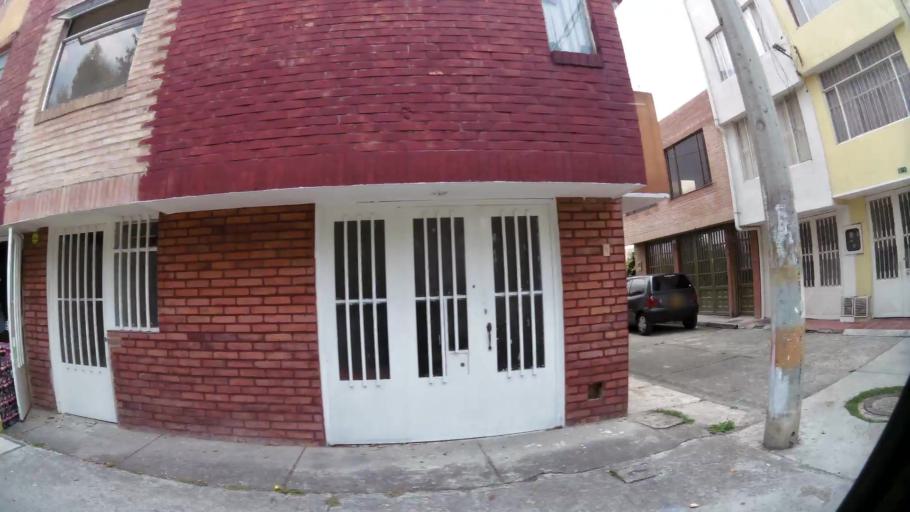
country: CO
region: Cundinamarca
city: Cota
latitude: 4.7455
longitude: -74.0621
